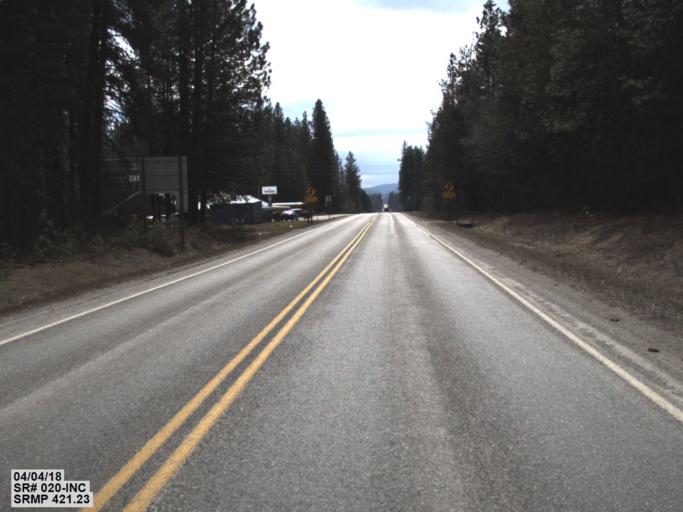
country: US
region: Washington
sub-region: Pend Oreille County
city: Newport
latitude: 48.3082
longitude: -117.2859
